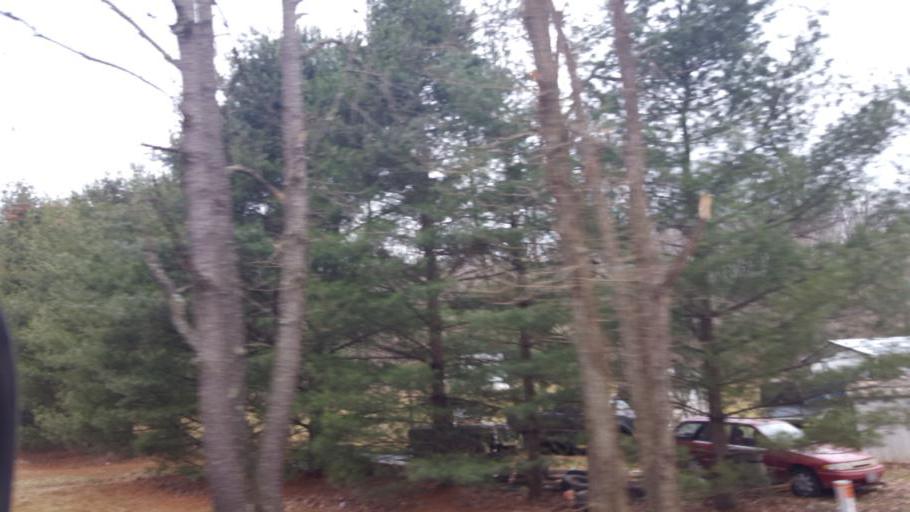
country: US
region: Ohio
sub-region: Ashland County
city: Loudonville
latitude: 40.5495
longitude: -82.2711
